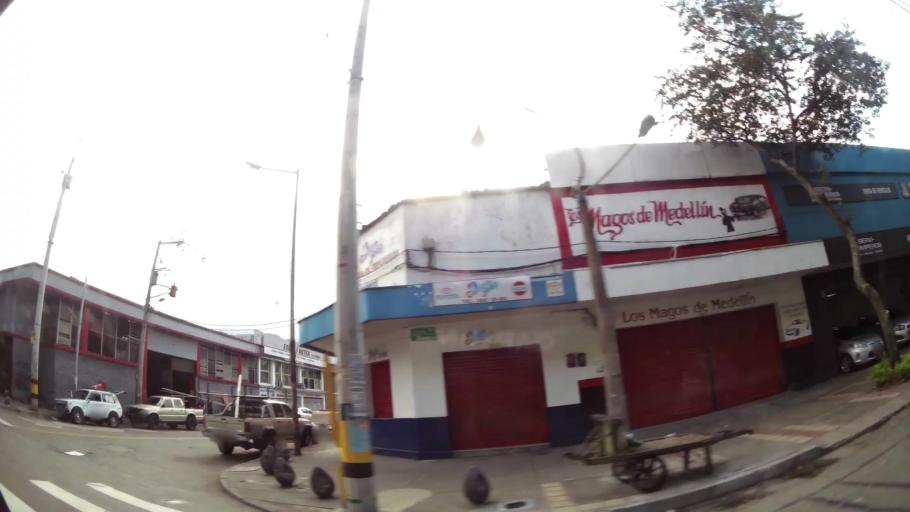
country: CO
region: Antioquia
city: Medellin
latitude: 6.2408
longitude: -75.5721
